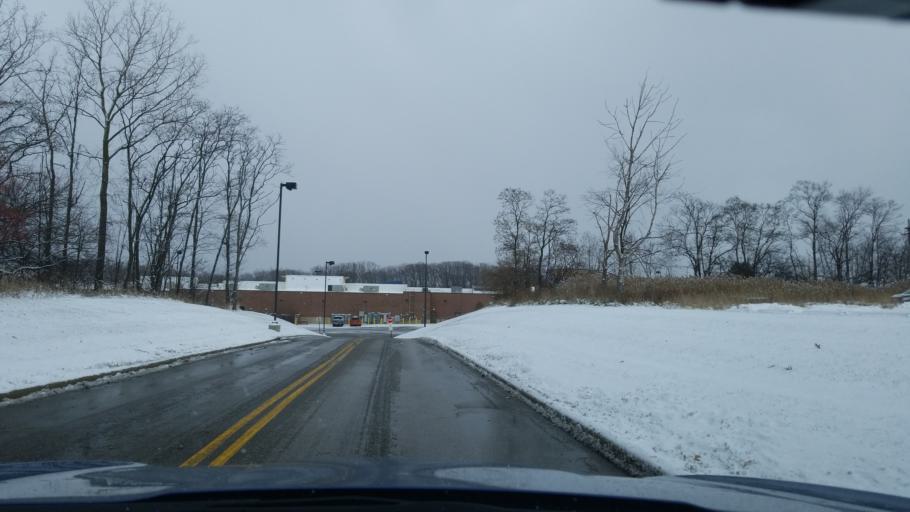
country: US
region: Ohio
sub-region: Cuyahoga County
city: Strongsville
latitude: 41.3148
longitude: -81.8194
